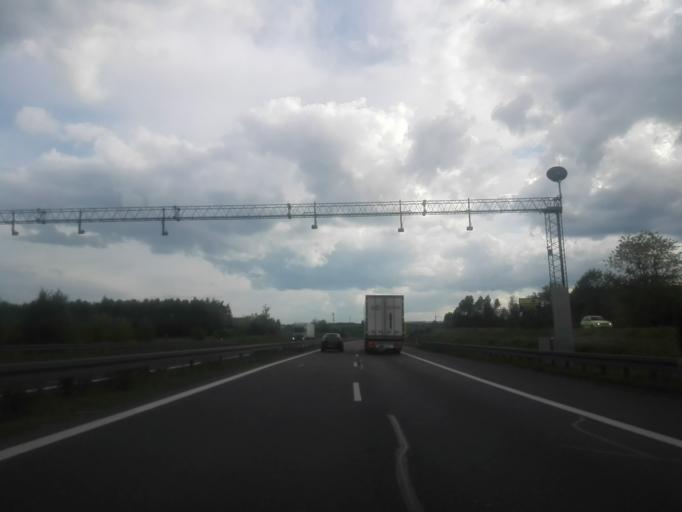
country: PL
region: Masovian Voivodeship
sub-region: Powiat ostrowski
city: Ostrow Mazowiecka
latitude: 52.8093
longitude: 21.8767
